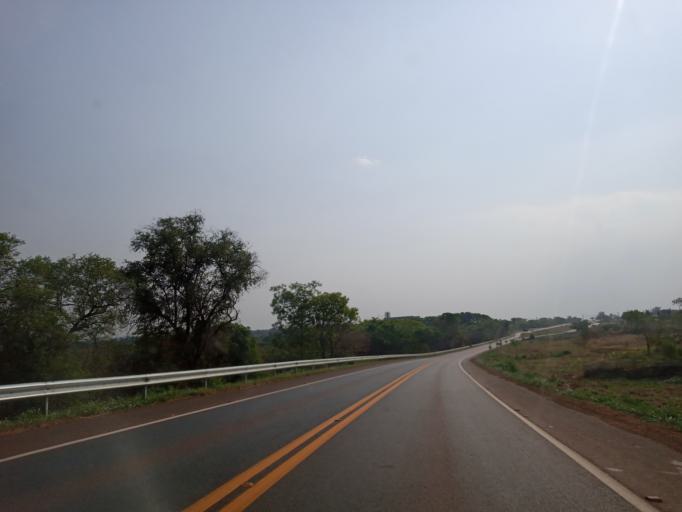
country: BR
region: Minas Gerais
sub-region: Ituiutaba
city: Ituiutaba
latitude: -18.9657
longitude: -49.4841
